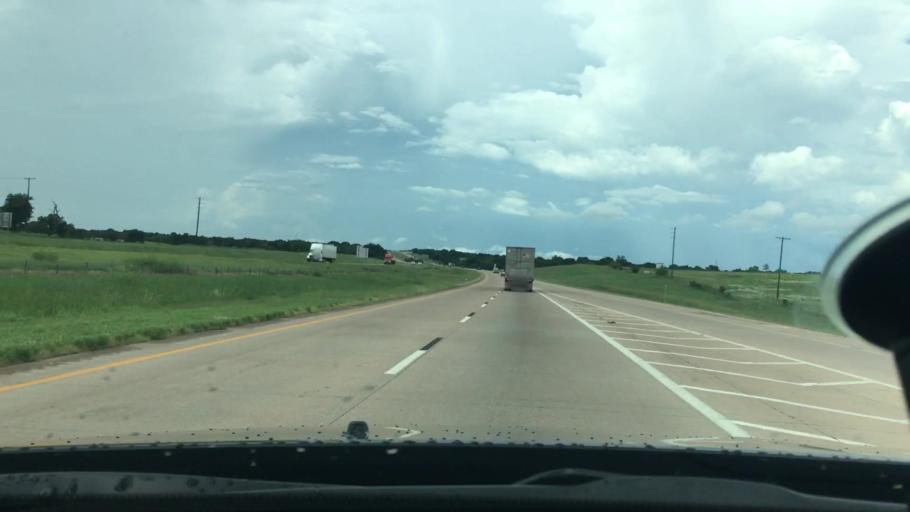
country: US
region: Oklahoma
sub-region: Garvin County
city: Wynnewood
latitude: 34.6545
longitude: -97.2203
